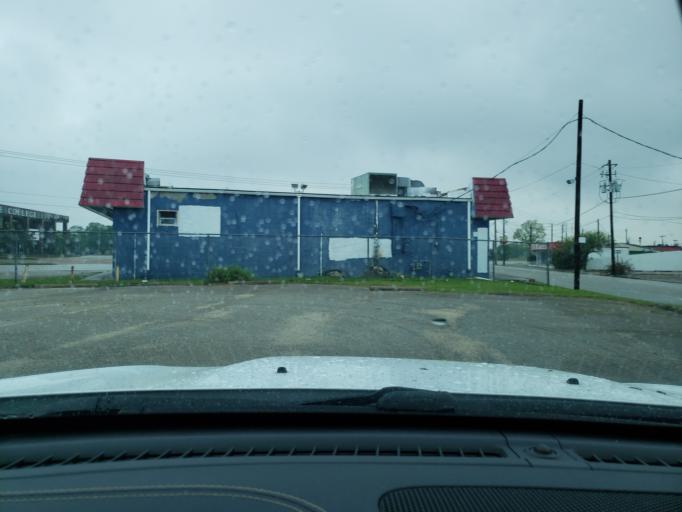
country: US
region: Texas
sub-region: Harris County
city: Baytown
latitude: 29.7366
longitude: -94.9771
